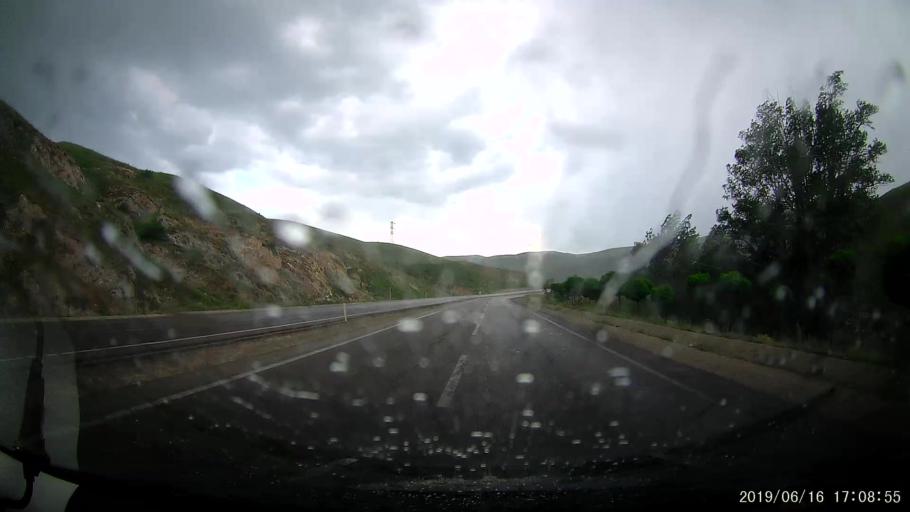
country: TR
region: Erzurum
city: Askale
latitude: 39.9017
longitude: 40.6563
